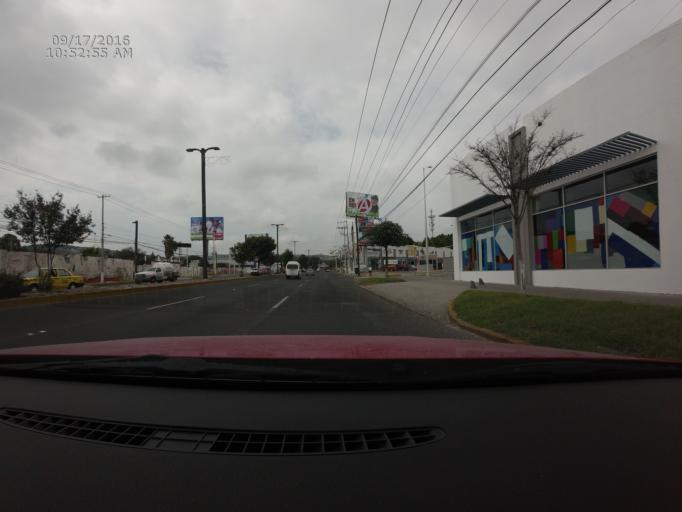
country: MX
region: Queretaro
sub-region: Corregidora
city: El Pueblito
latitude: 20.5345
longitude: -100.4374
